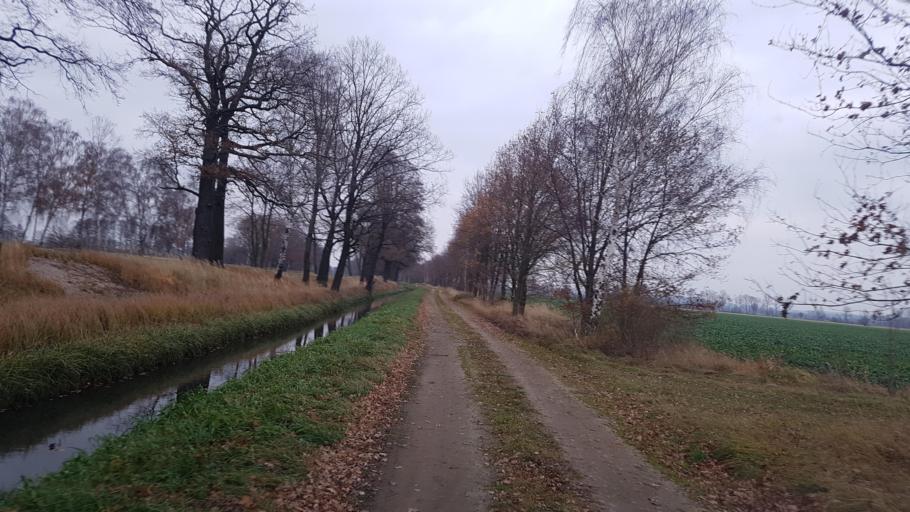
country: DE
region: Brandenburg
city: Hirschfeld
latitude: 51.4137
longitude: 13.6114
